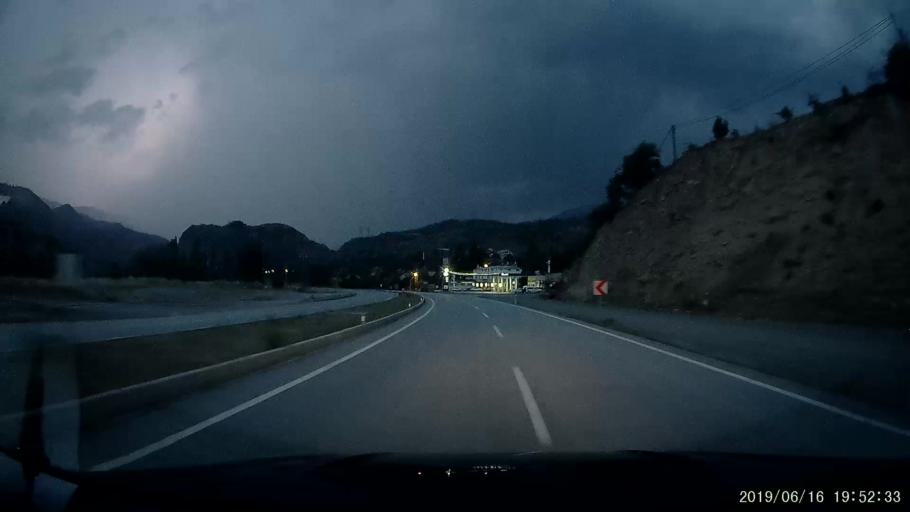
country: TR
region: Sivas
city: Koyulhisar
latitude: 40.2884
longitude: 37.8020
